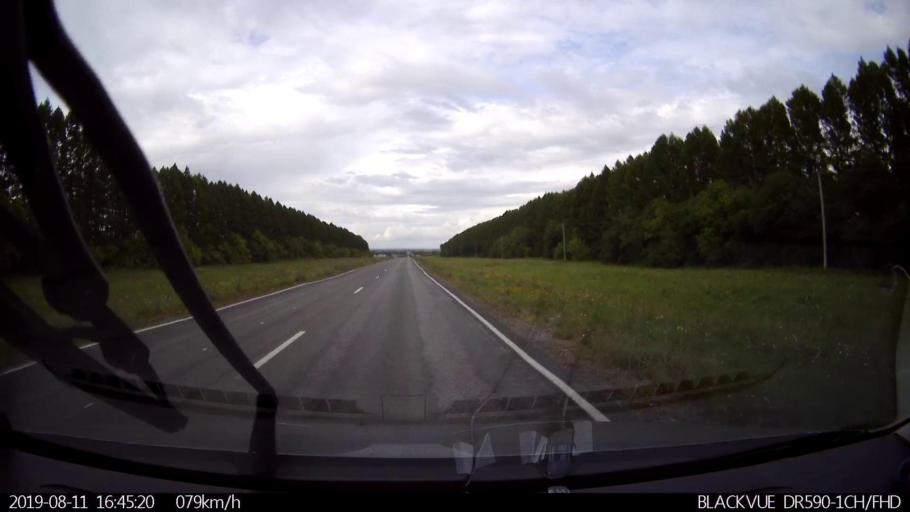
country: RU
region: Ulyanovsk
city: Mayna
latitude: 54.1887
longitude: 47.6854
